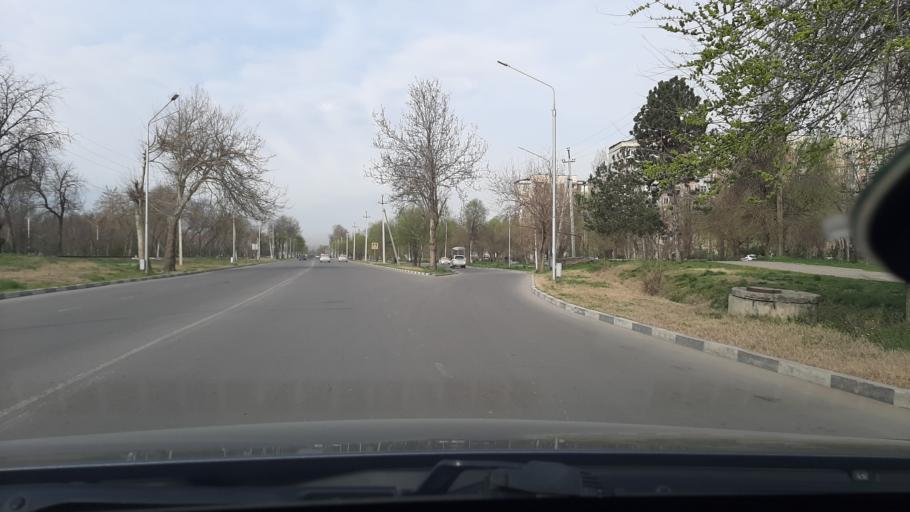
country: TJ
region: Dushanbe
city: Dushanbe
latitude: 38.5692
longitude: 68.7519
